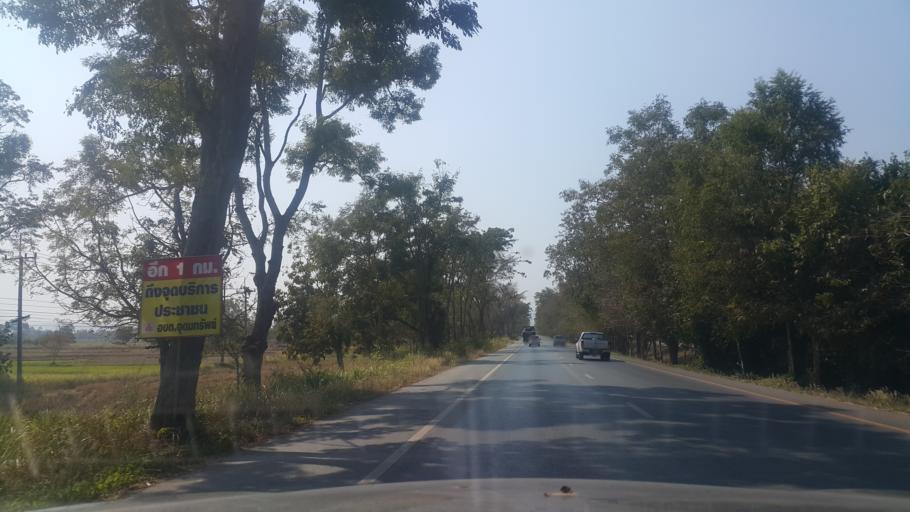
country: TH
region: Nakhon Ratchasima
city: Wang Nam Khiao
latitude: 14.5487
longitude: 101.9724
